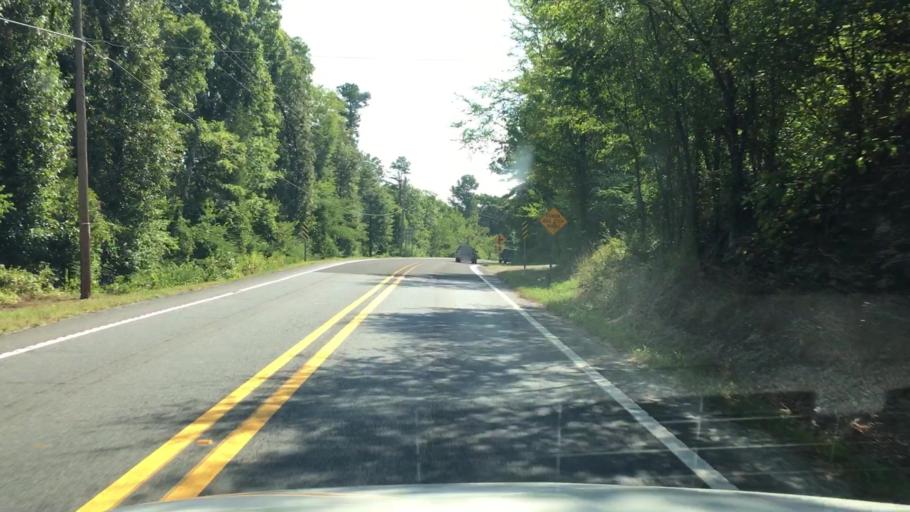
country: US
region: Arkansas
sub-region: Garland County
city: Piney
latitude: 34.5095
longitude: -93.1743
